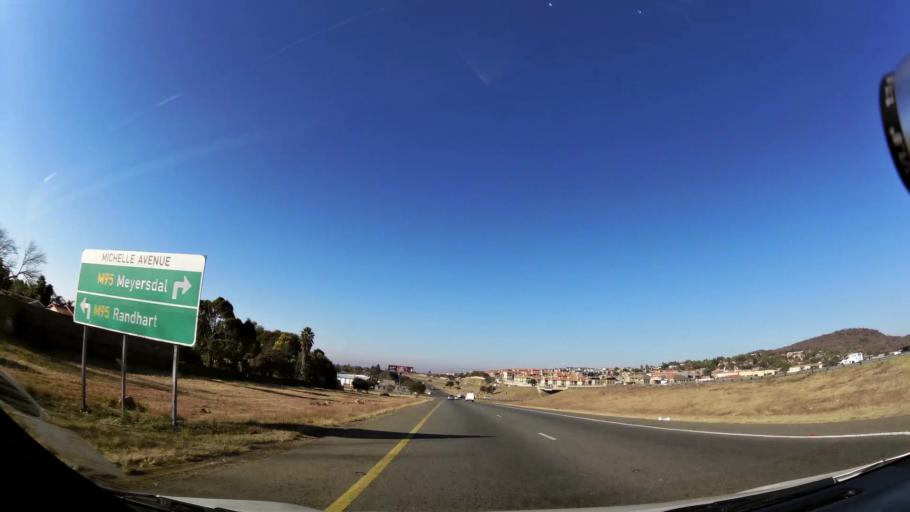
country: ZA
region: Gauteng
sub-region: Ekurhuleni Metropolitan Municipality
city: Germiston
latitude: -26.2849
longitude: 28.1019
